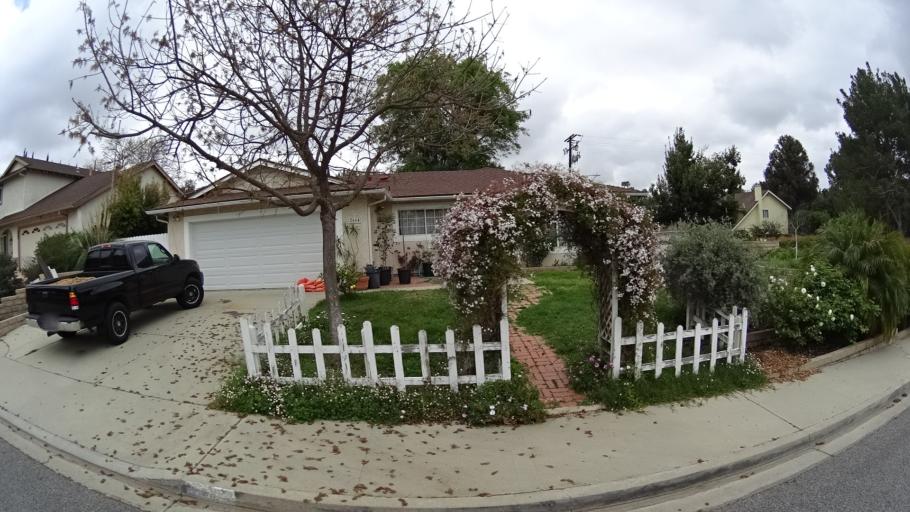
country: US
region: California
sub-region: Ventura County
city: Casa Conejo
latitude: 34.2155
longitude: -118.8862
